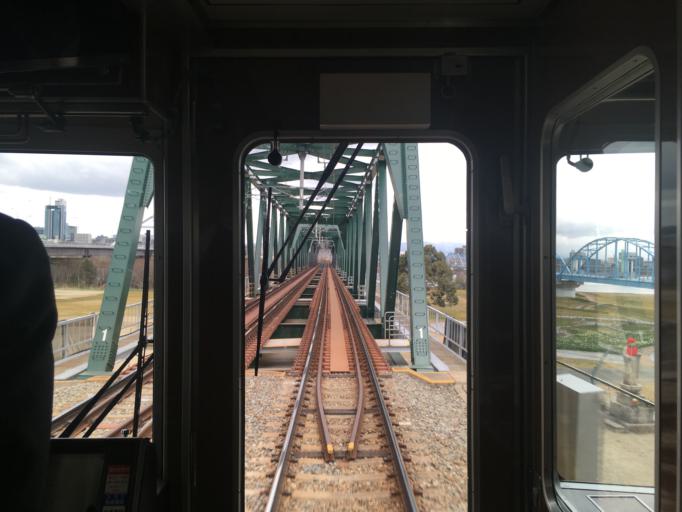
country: JP
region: Osaka
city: Osaka-shi
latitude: 34.7188
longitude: 135.5118
